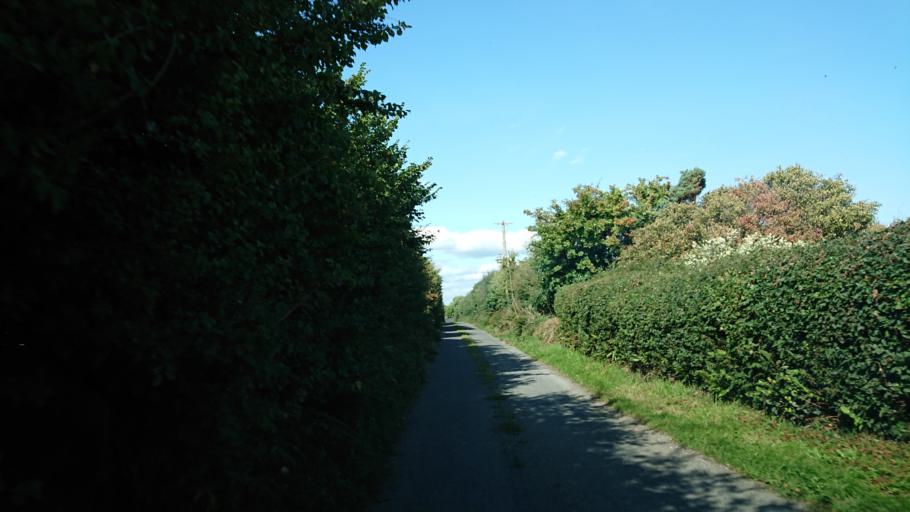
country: IE
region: Munster
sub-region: Waterford
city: Waterford
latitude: 52.2102
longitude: -7.0552
